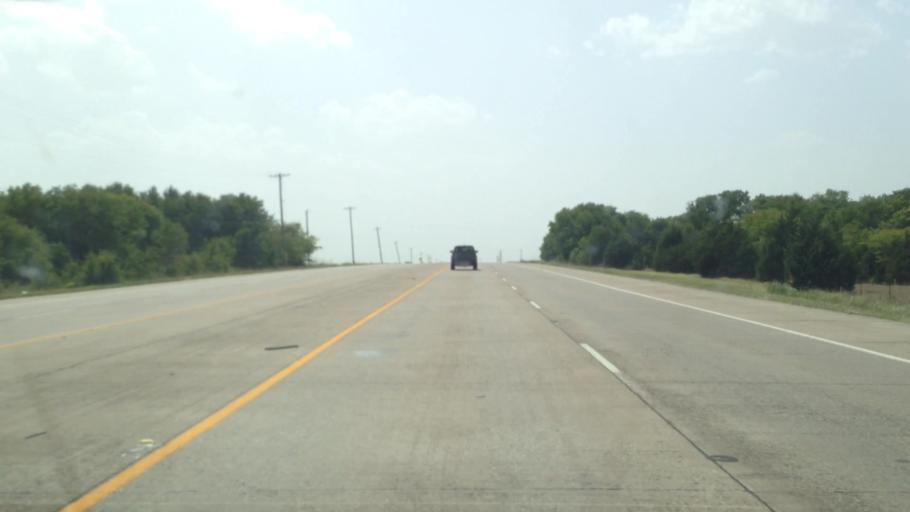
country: US
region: Texas
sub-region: Collin County
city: Princeton
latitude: 33.1710
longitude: -96.4767
